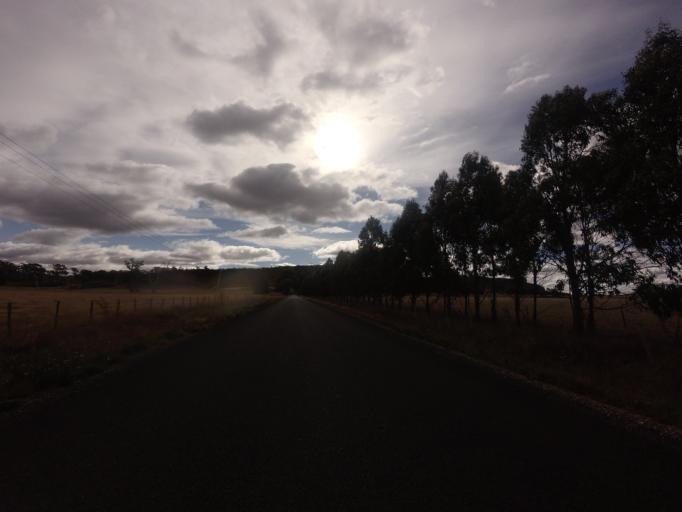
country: AU
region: Tasmania
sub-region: Brighton
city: Bridgewater
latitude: -42.4007
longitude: 147.3890
